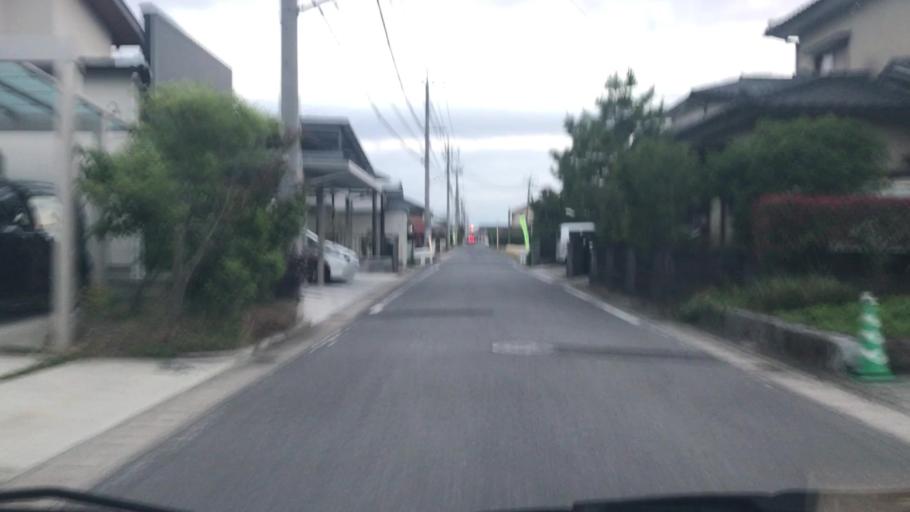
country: JP
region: Saga Prefecture
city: Saga-shi
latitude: 33.2311
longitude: 130.3018
